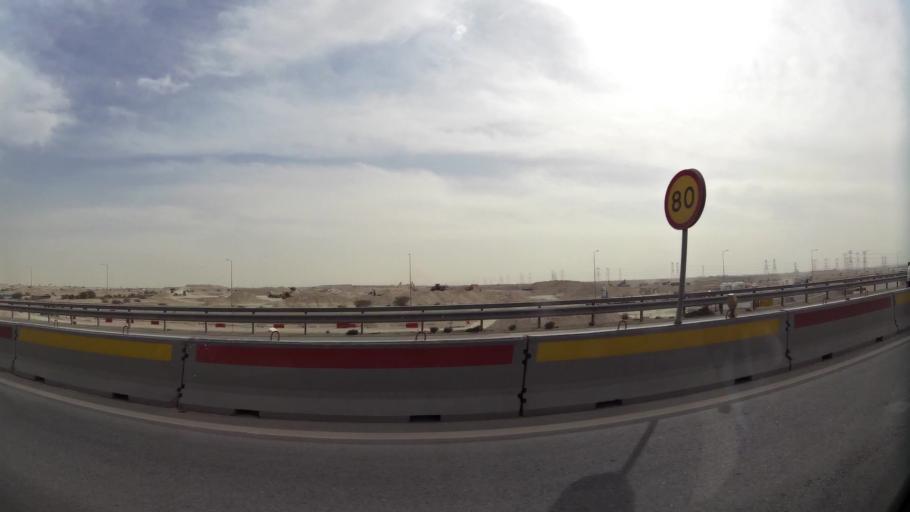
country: QA
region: Baladiyat ar Rayyan
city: Ash Shahaniyah
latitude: 25.3355
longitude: 51.3265
